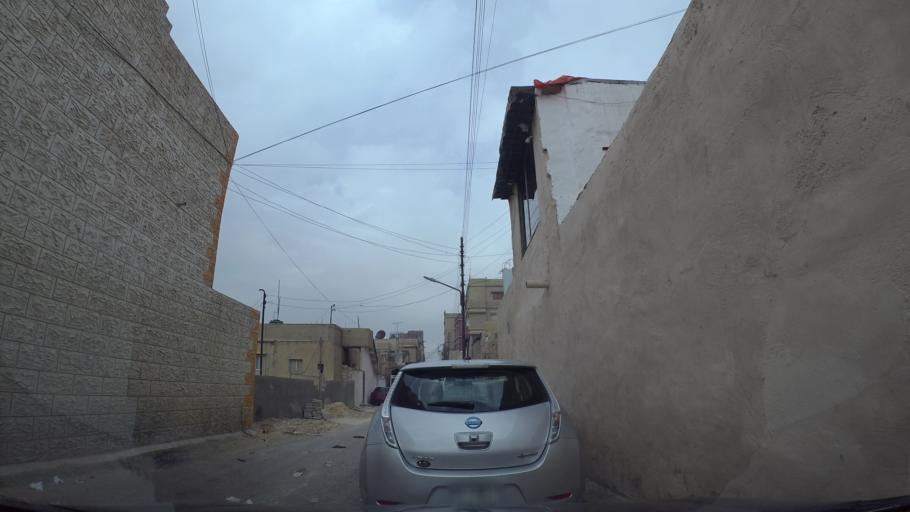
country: JO
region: Amman
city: Amman
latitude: 31.9572
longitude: 35.9402
